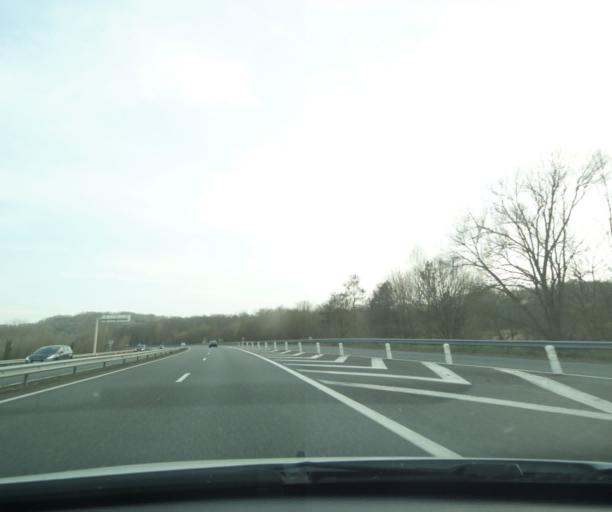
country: FR
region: Midi-Pyrenees
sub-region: Departement des Hautes-Pyrenees
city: Tournay
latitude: 43.1815
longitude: 0.2238
